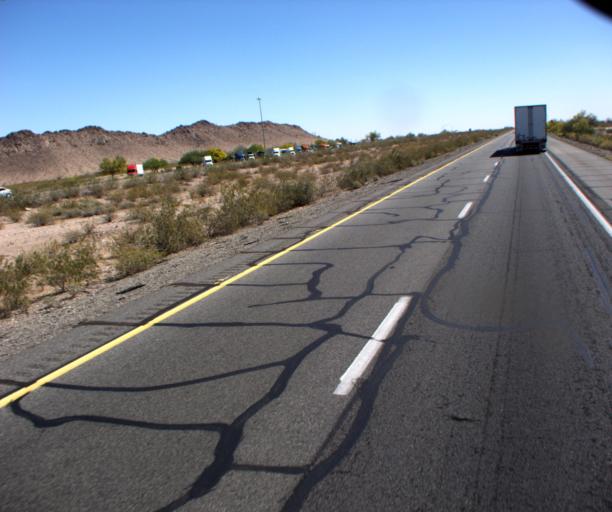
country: US
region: Arizona
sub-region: Maricopa County
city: Buckeye
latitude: 33.5205
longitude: -113.0707
